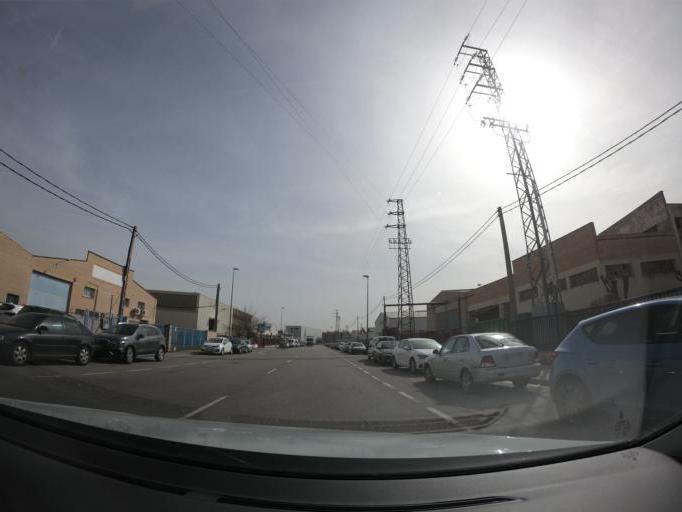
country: ES
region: Basque Country
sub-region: Provincia de Alava
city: Oyon
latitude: 42.4764
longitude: -2.4041
